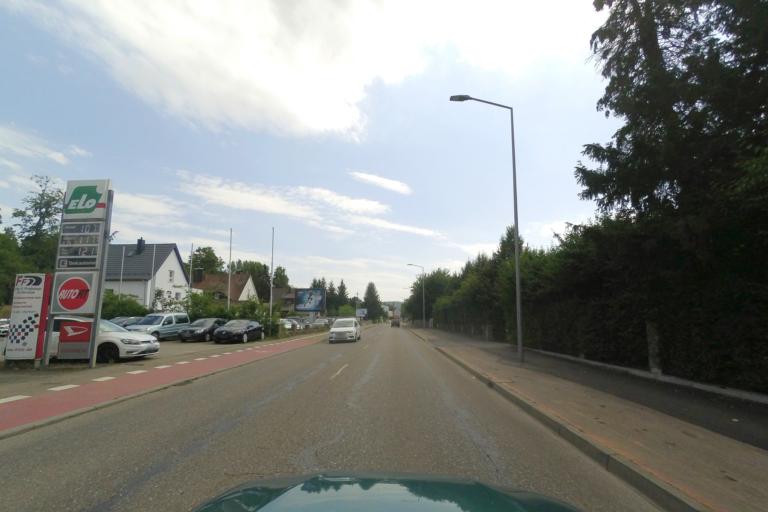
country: DE
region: Baden-Wuerttemberg
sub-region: Regierungsbezirk Stuttgart
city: Aalen
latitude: 48.8547
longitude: 10.1007
